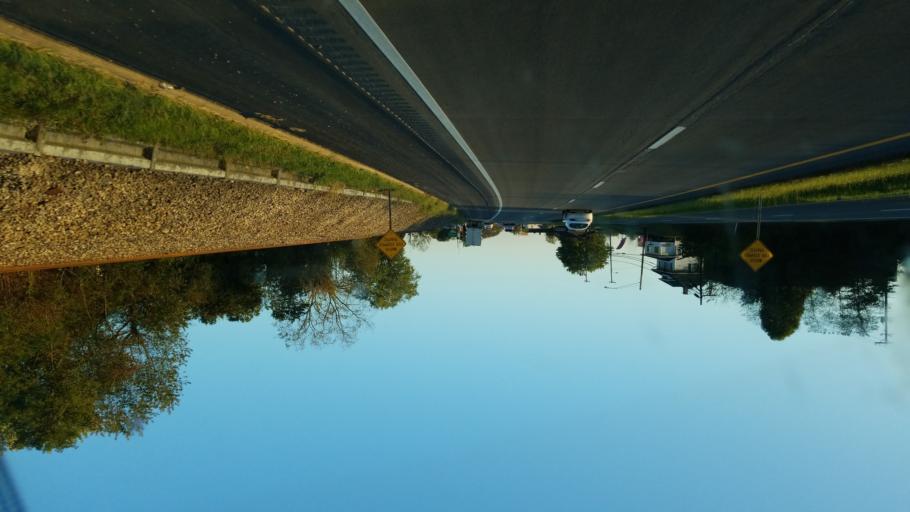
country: US
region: Ohio
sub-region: Scioto County
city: Lucasville
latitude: 38.8723
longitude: -82.9950
